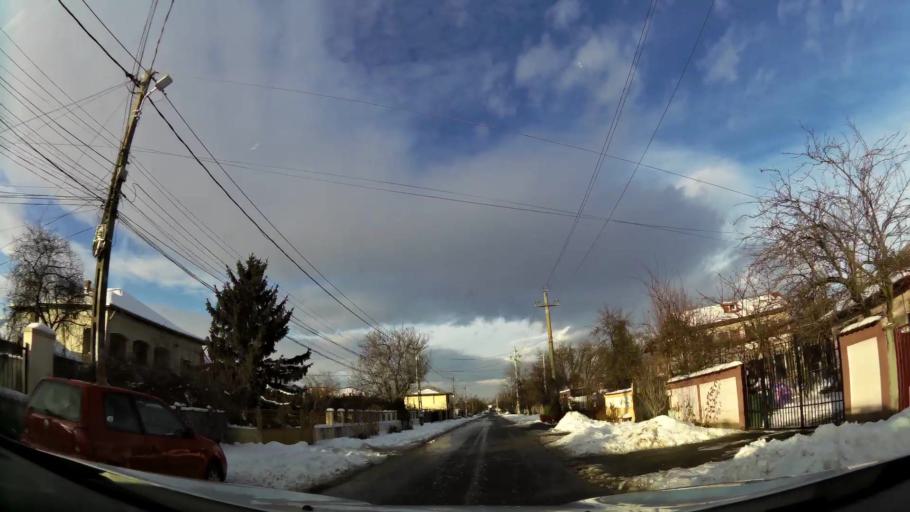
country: RO
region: Ilfov
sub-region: Comuna Jilava
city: Jilava
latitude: 44.3377
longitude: 26.0832
